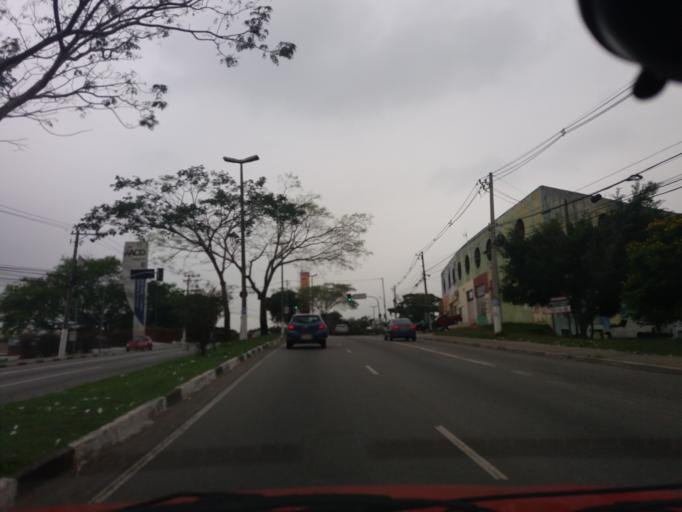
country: BR
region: Sao Paulo
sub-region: Osasco
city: Osasco
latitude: -23.5079
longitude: -46.7887
